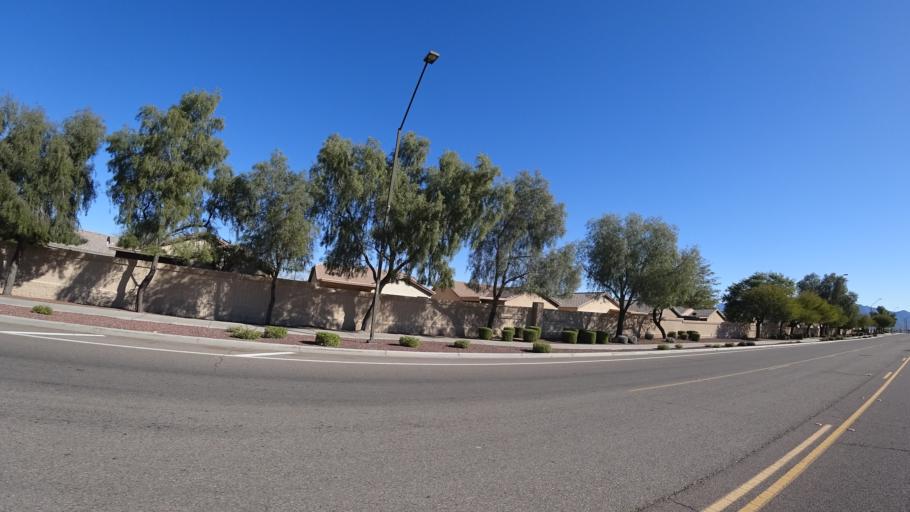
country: US
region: Arizona
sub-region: Maricopa County
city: Goodyear
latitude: 33.4239
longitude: -112.3579
